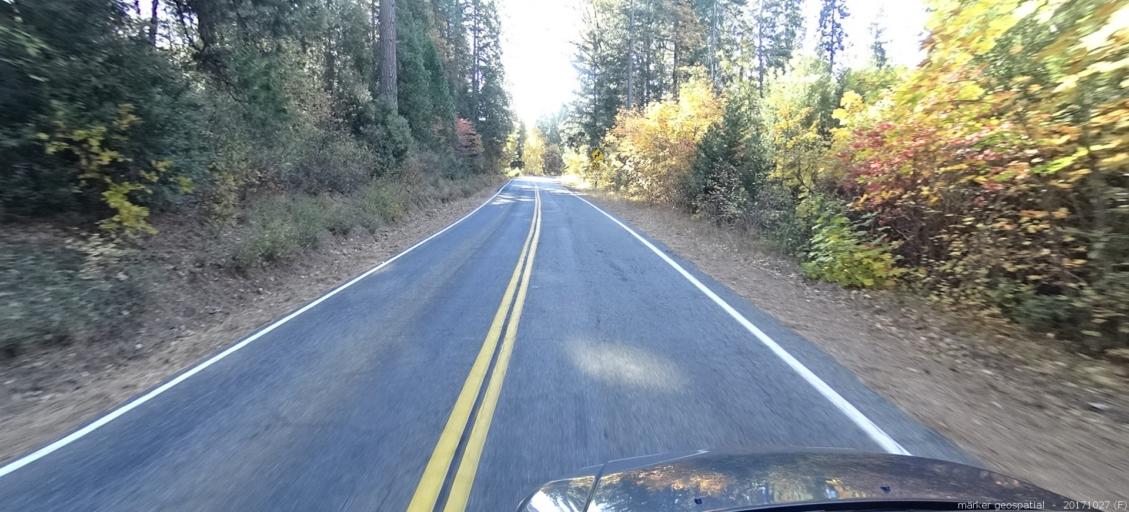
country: US
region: California
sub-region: Shasta County
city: Burney
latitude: 40.8879
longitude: -121.9073
